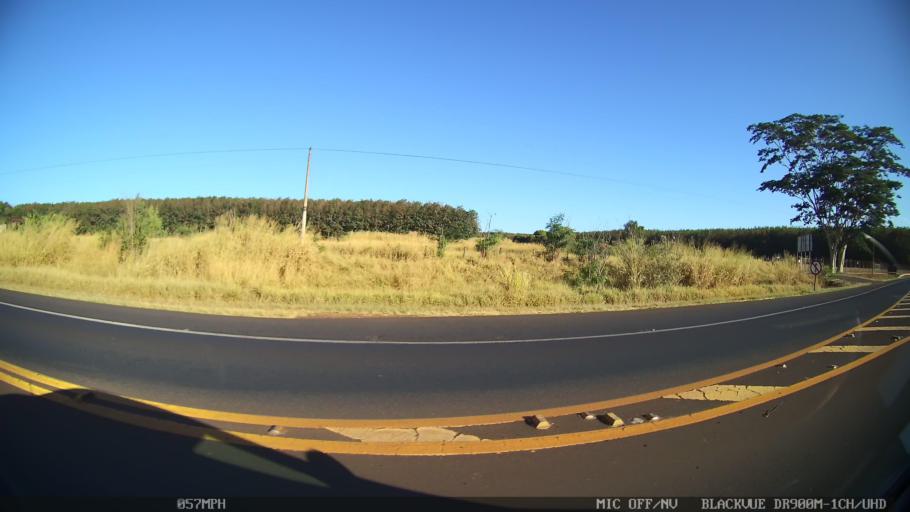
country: BR
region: Sao Paulo
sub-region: Guapiacu
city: Guapiacu
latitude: -20.7520
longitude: -49.1406
